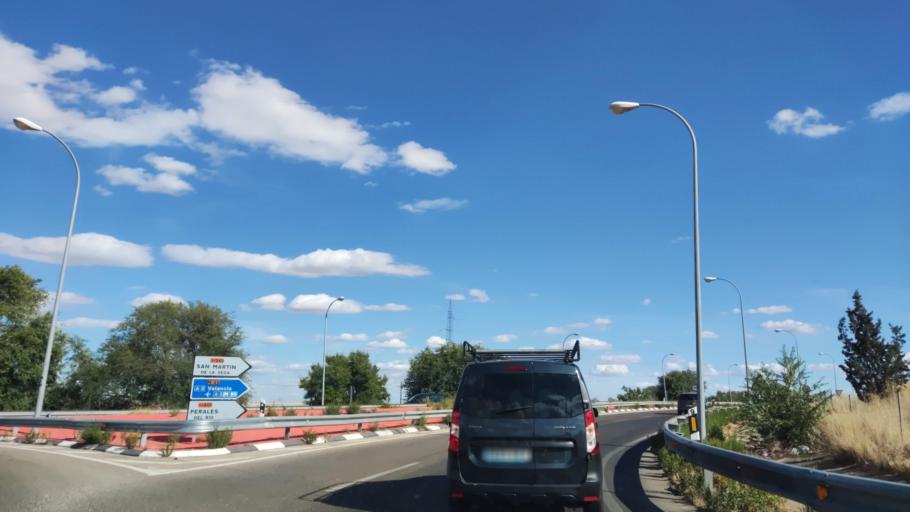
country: ES
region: Madrid
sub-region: Provincia de Madrid
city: Villaverde
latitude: 40.3377
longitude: -3.6680
